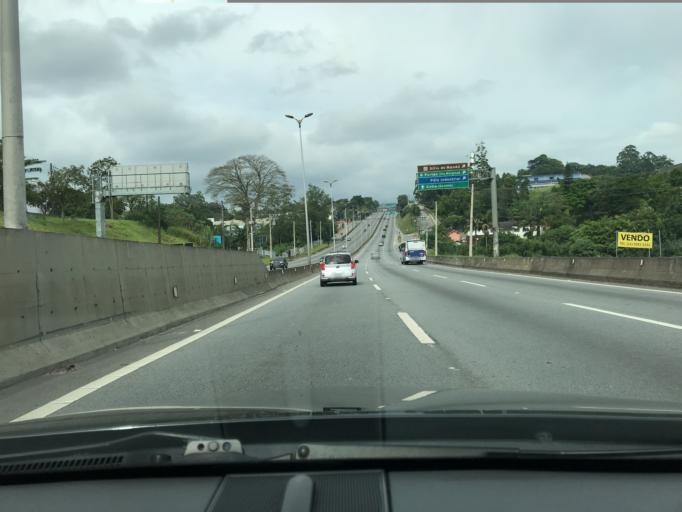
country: BR
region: Sao Paulo
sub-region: Cotia
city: Cotia
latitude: -23.5989
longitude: -46.8931
